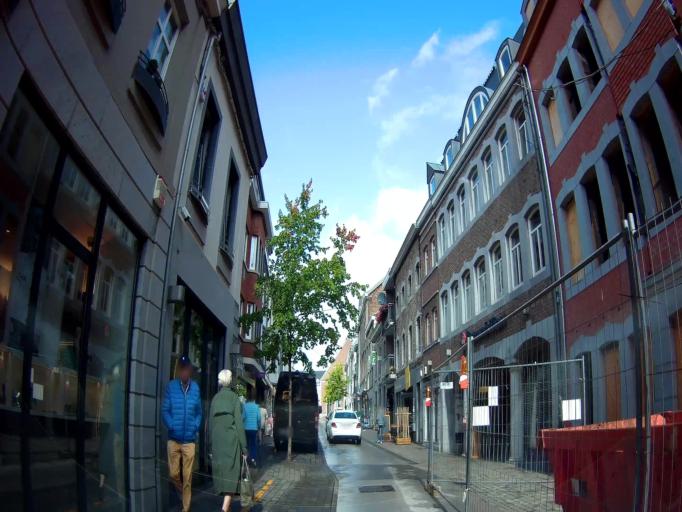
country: BE
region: Wallonia
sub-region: Province de Liege
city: Eupen
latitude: 50.6314
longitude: 6.0307
